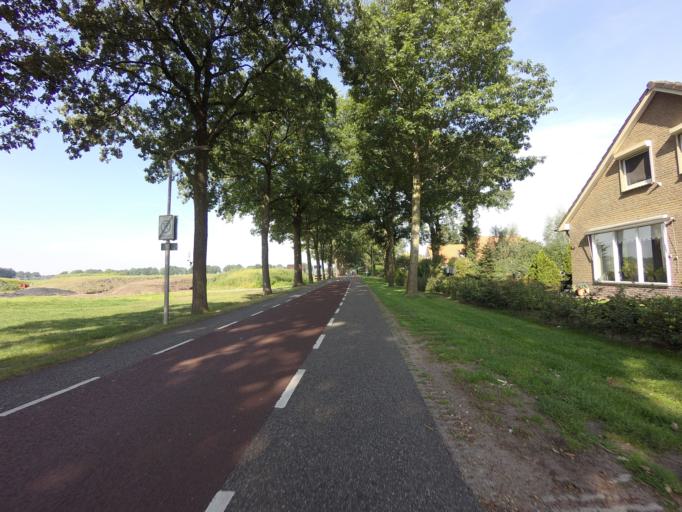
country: NL
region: Overijssel
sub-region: Gemeente Hardenberg
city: Hardenberg
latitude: 52.5676
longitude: 6.6594
